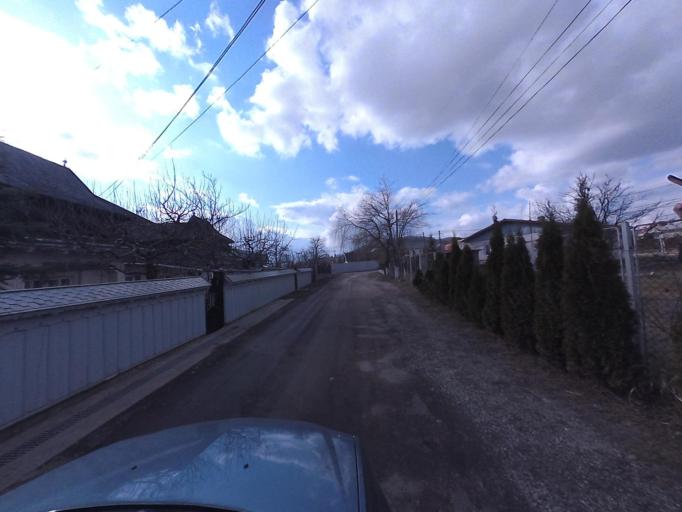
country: RO
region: Neamt
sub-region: Oras Targu Neamt
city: Targu Neamt
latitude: 47.2119
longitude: 26.3790
